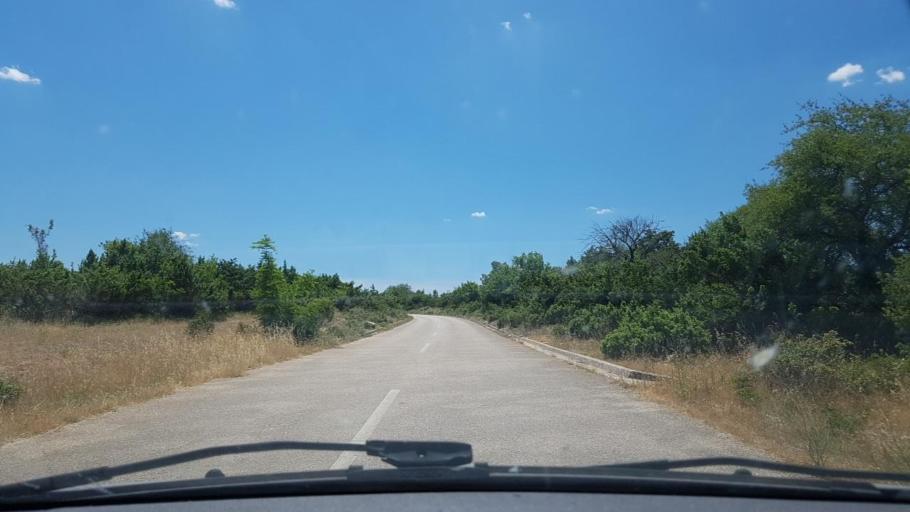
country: HR
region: Sibensko-Kniniska
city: Kistanje
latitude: 43.9771
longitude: 15.9712
